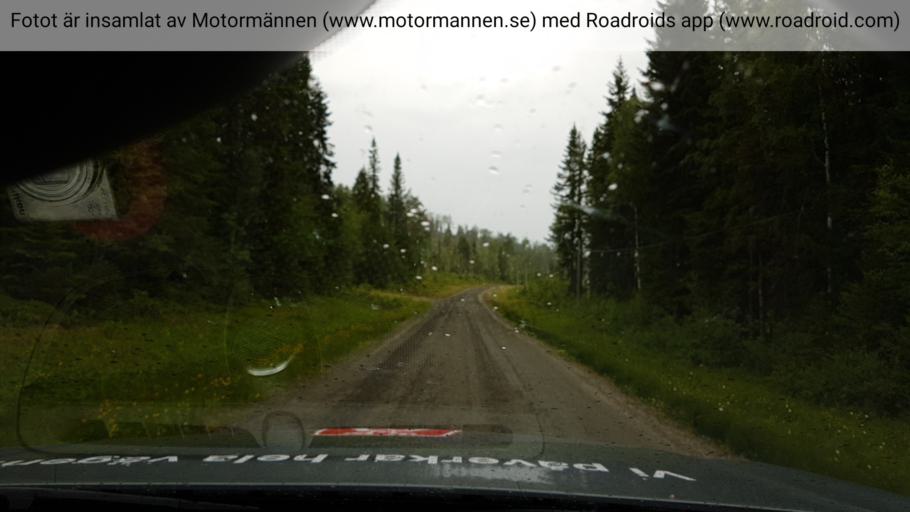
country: SE
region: Jaemtland
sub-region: Bergs Kommun
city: Hoverberg
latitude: 62.5338
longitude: 14.7049
